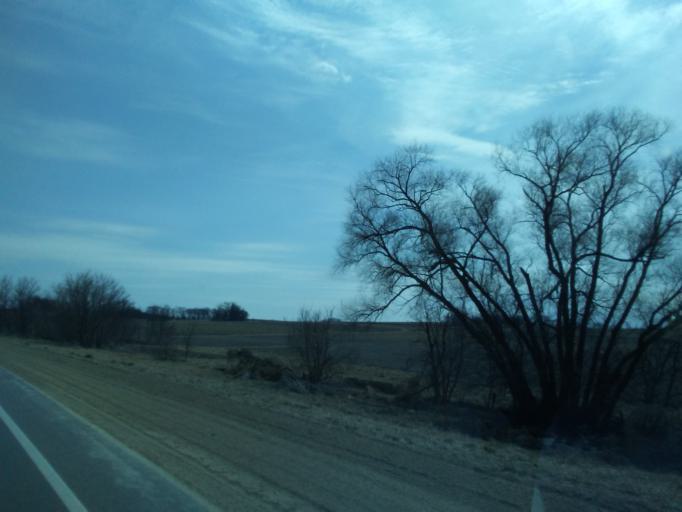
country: US
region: Iowa
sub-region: Winneshiek County
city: Decorah
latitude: 43.4070
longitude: -91.8545
